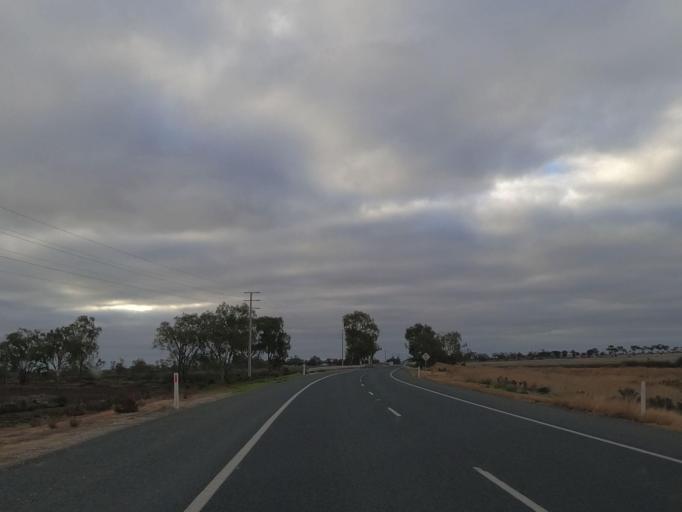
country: AU
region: Victoria
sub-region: Swan Hill
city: Swan Hill
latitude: -35.6204
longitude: 143.8035
